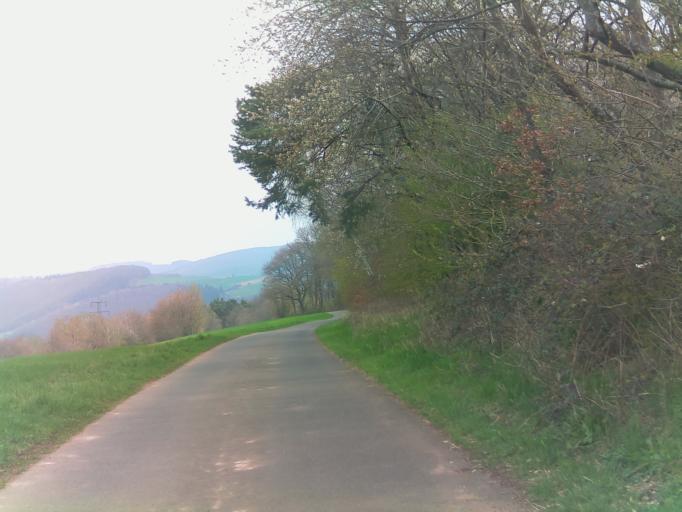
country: DE
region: Rheinland-Pfalz
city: Gerach
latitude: 49.7548
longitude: 7.3245
